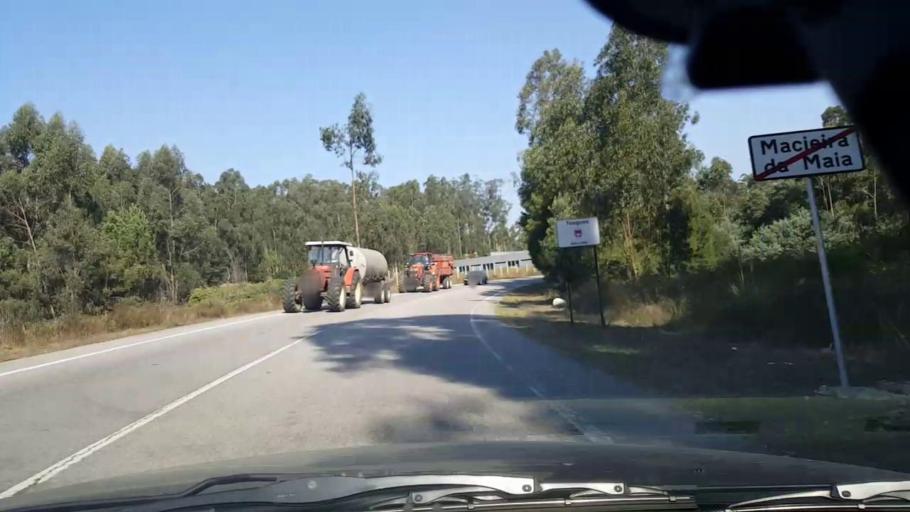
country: PT
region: Porto
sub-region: Vila do Conde
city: Arvore
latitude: 41.3541
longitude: -8.6876
